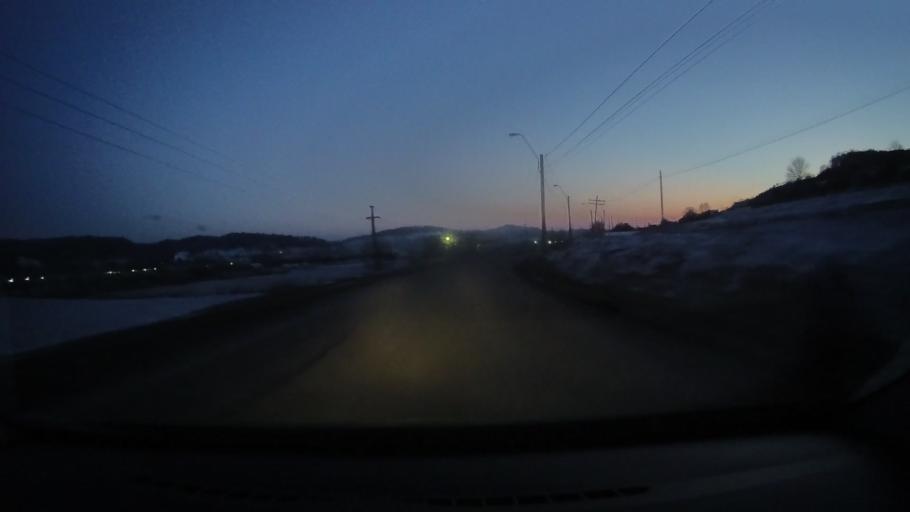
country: RO
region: Sibiu
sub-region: Municipiul Medias
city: Medias
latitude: 46.1805
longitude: 24.3690
